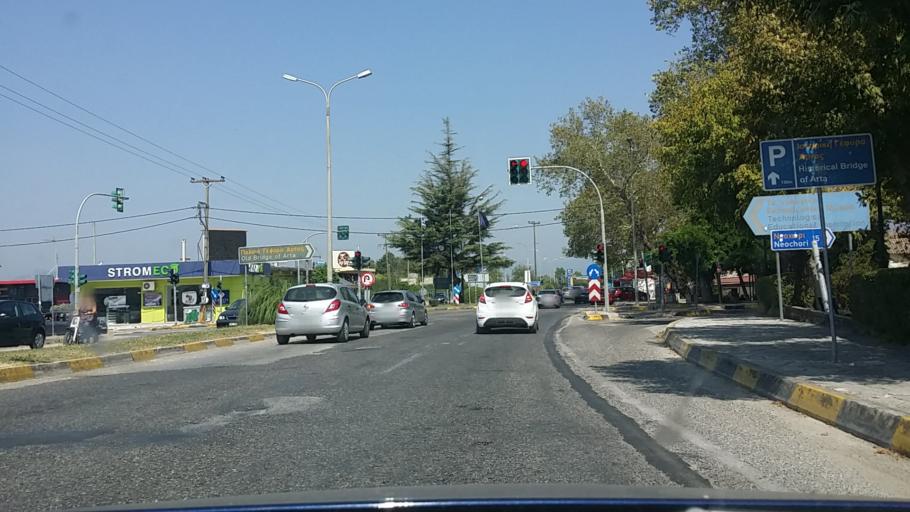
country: GR
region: Epirus
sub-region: Nomos Artas
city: Arta
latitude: 39.1507
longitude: 20.9735
